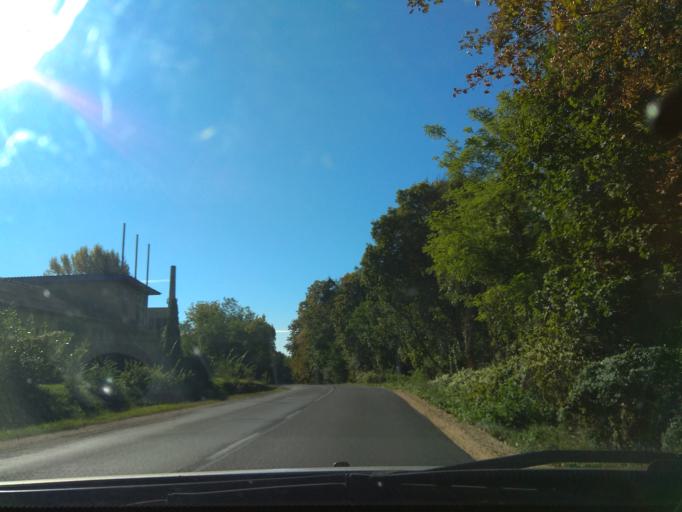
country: HU
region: Borsod-Abauj-Zemplen
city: Miskolc
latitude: 48.0811
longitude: 20.7714
